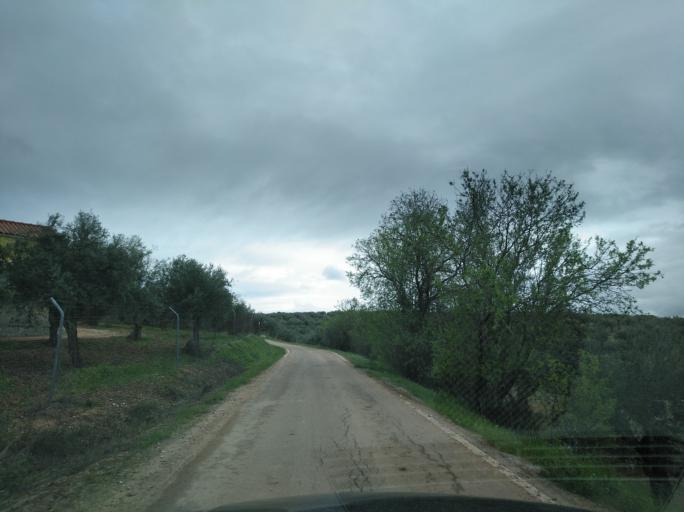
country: PT
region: Portalegre
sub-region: Campo Maior
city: Campo Maior
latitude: 38.9887
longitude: -7.0454
